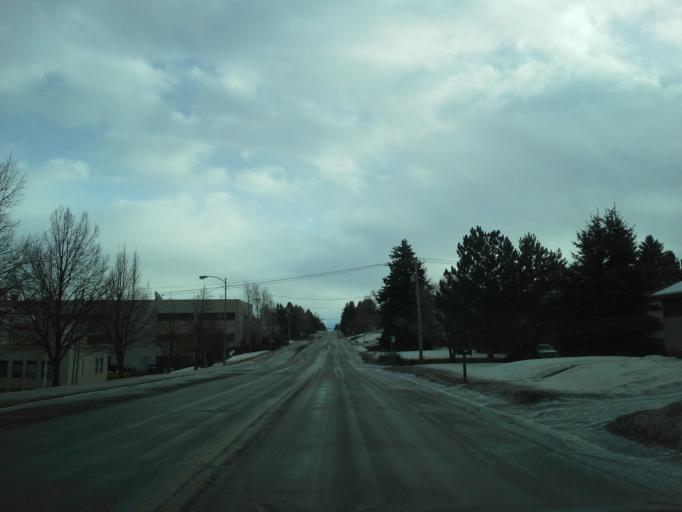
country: US
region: Montana
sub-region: Lewis and Clark County
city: Helena
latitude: 46.5841
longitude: -112.0175
